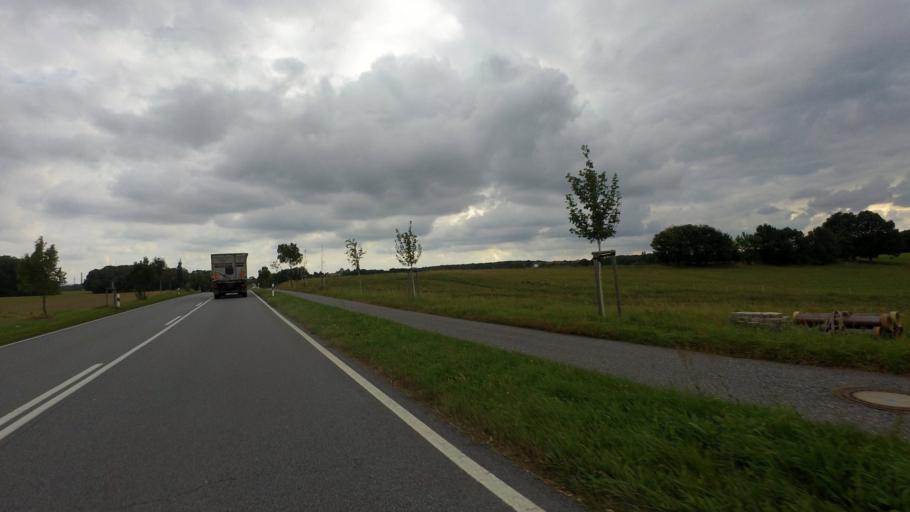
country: DE
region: Saxony
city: Radibor
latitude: 51.2205
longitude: 14.3893
